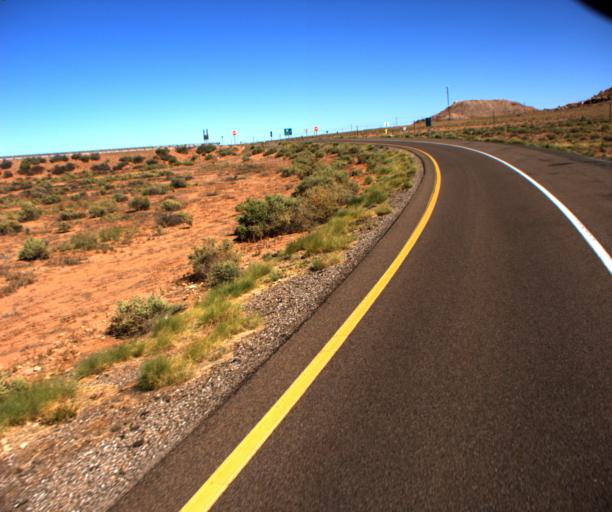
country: US
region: Arizona
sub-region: Coconino County
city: LeChee
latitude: 35.0682
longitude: -110.8333
